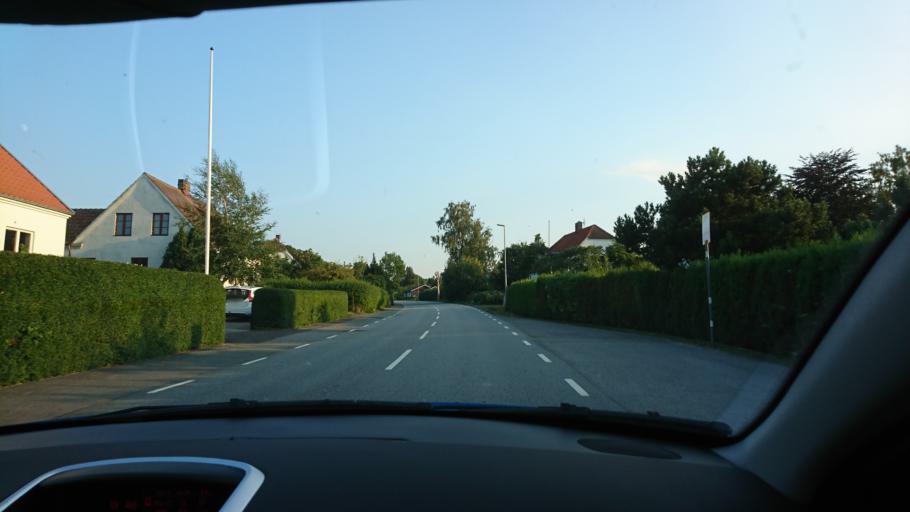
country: SE
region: Skane
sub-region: Simrishamns Kommun
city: Kivik
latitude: 55.7114
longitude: 14.1522
